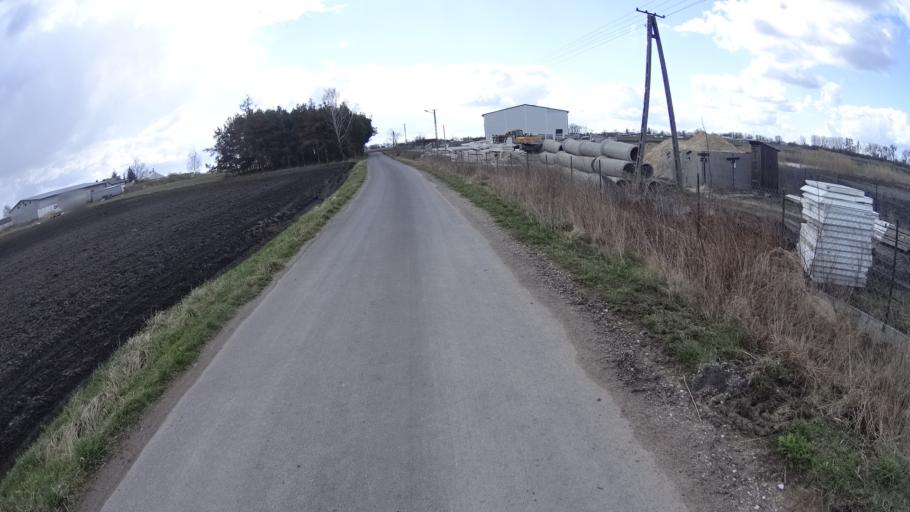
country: PL
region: Masovian Voivodeship
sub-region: Powiat warszawski zachodni
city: Jozefow
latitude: 52.2255
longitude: 20.7258
